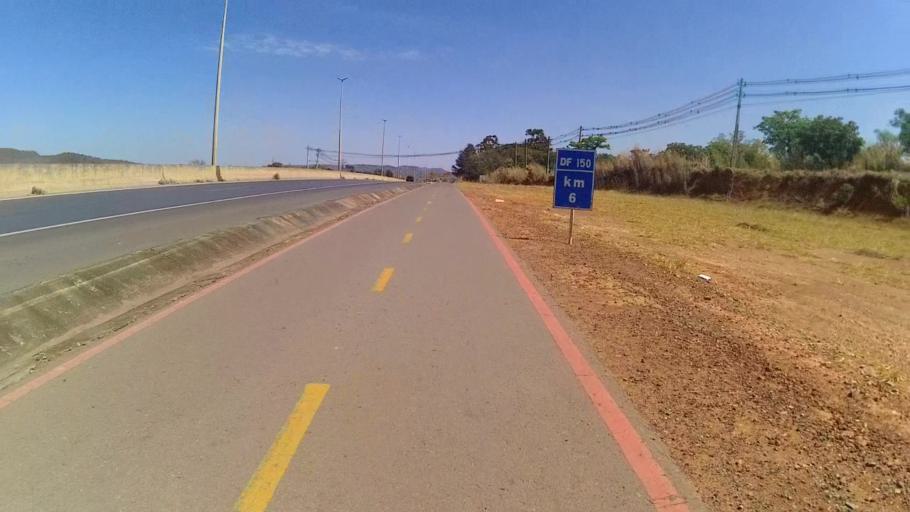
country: BR
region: Federal District
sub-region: Brasilia
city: Brasilia
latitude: -15.6476
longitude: -47.8455
